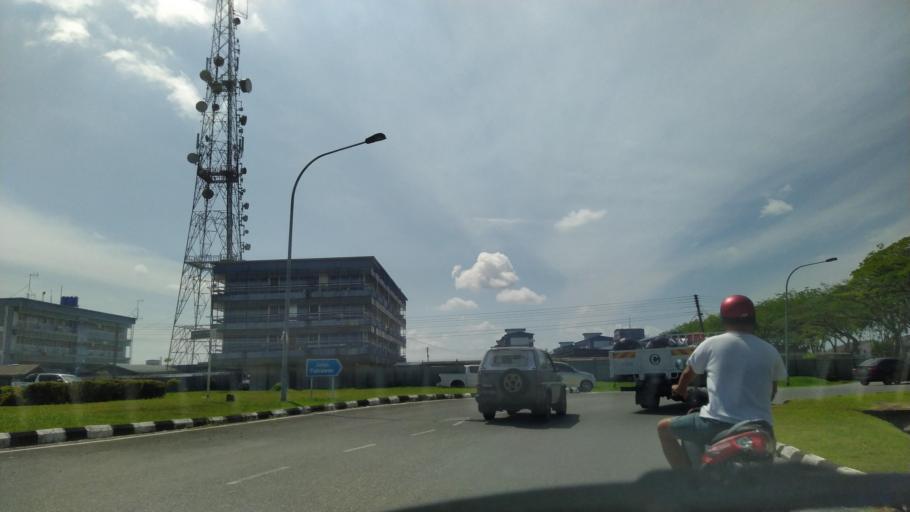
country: MY
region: Sarawak
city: Sibu
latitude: 2.3131
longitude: 111.8309
